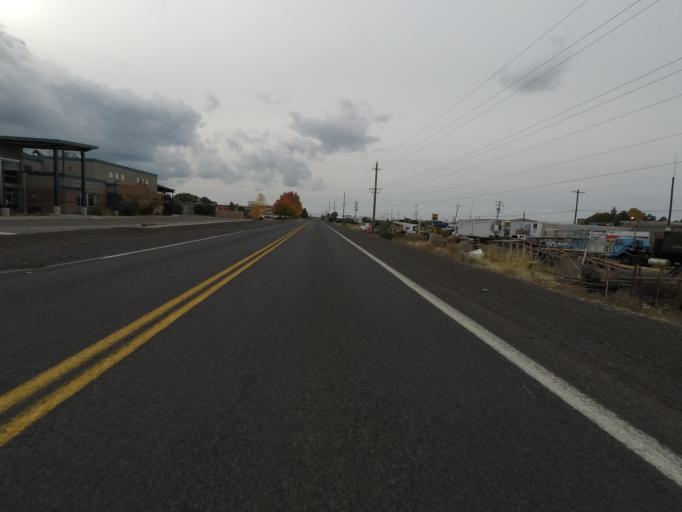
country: US
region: Washington
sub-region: Walla Walla County
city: Walla Walla East
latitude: 46.0812
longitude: -118.2792
